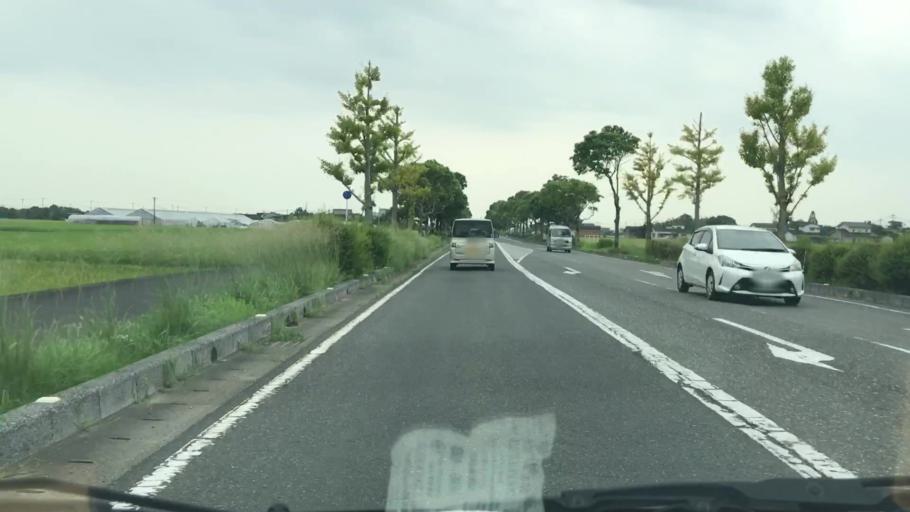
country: JP
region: Saga Prefecture
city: Saga-shi
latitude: 33.2283
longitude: 130.3062
